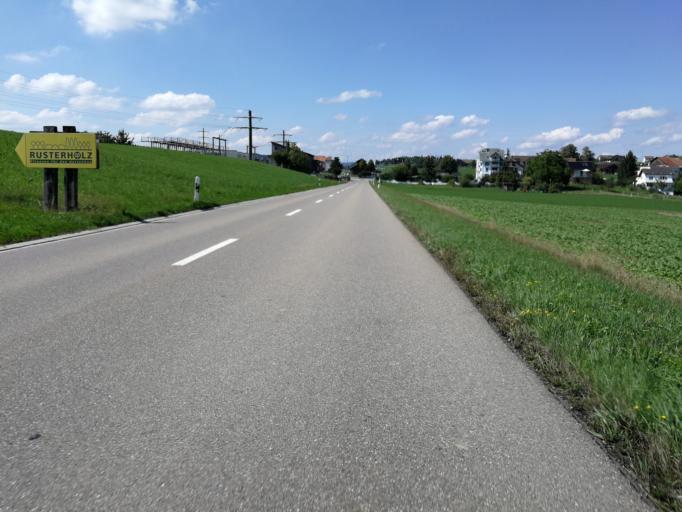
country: CH
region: Zurich
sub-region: Bezirk Horgen
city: Waedenswil / Eichweid
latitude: 47.2055
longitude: 8.6655
